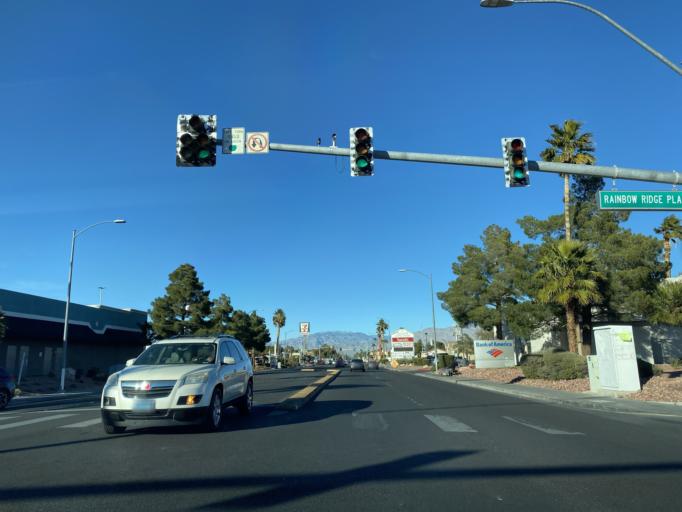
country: US
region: Nevada
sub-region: Clark County
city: Spring Valley
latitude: 36.2162
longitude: -115.2423
